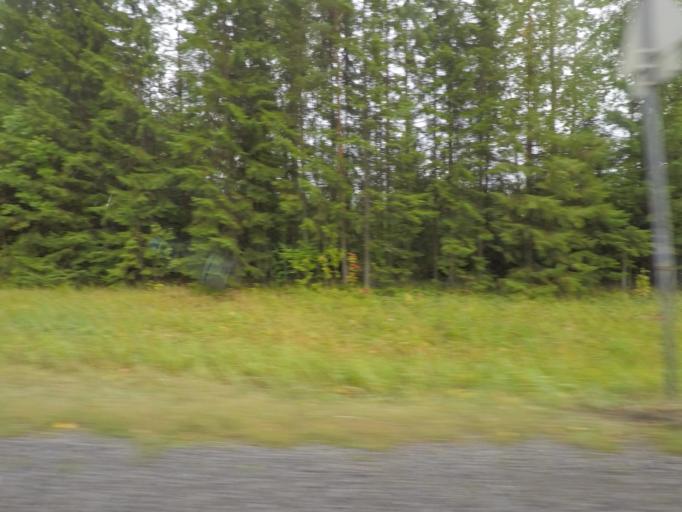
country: FI
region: Southern Savonia
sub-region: Pieksaemaeki
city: Joroinen
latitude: 62.0622
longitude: 27.8102
